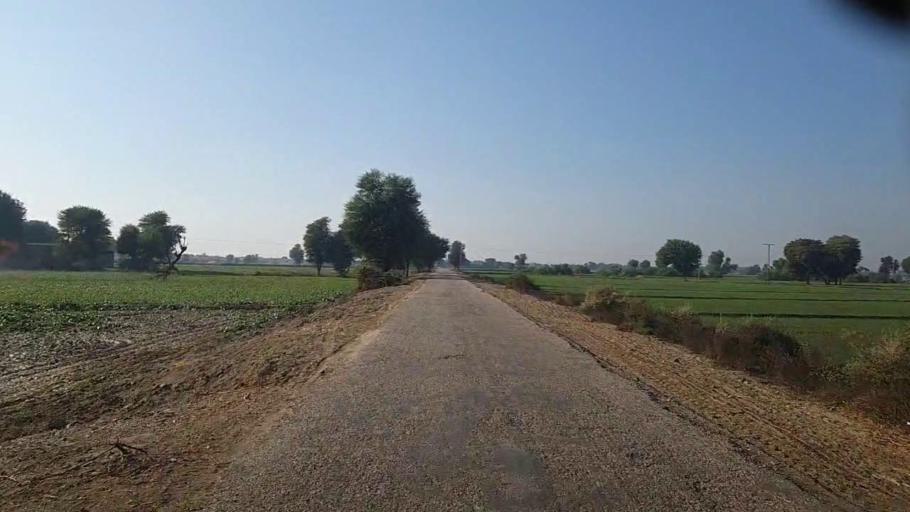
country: PK
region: Sindh
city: Darya Khan Marri
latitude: 26.6851
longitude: 68.3549
